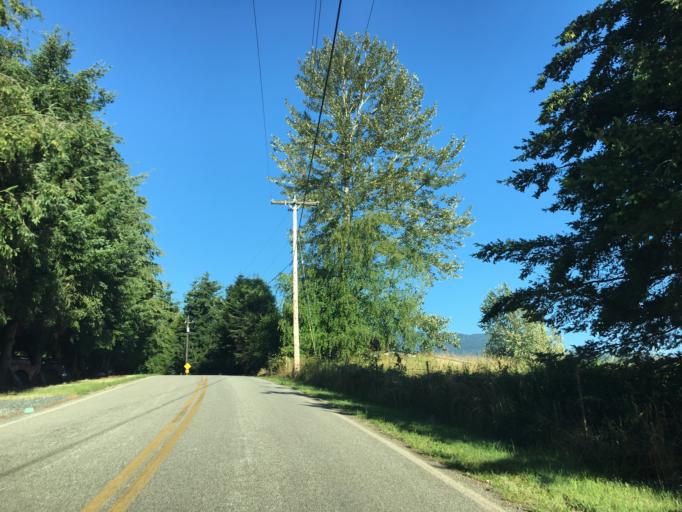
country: US
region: Washington
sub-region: Whatcom County
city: Nooksack
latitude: 48.9422
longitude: -122.3052
